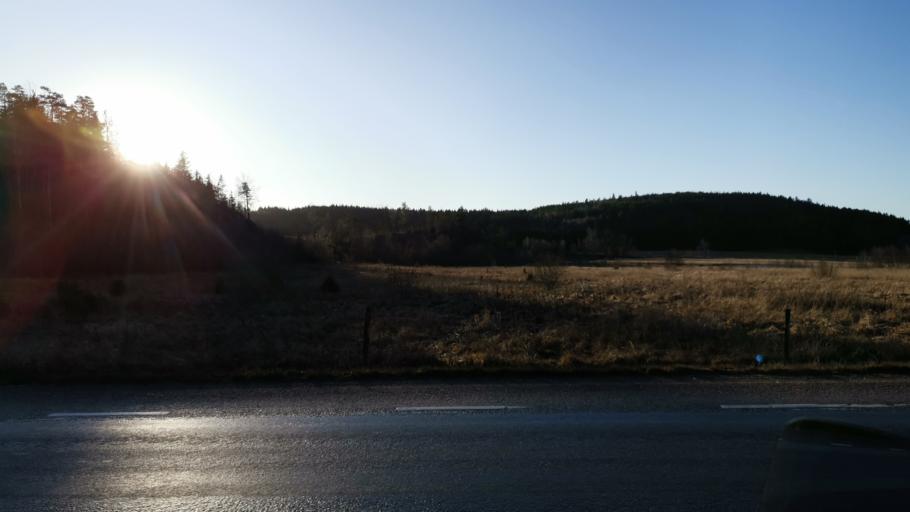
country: SE
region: Vaestra Goetaland
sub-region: Munkedals Kommun
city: Munkedal
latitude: 58.4805
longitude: 11.6418
